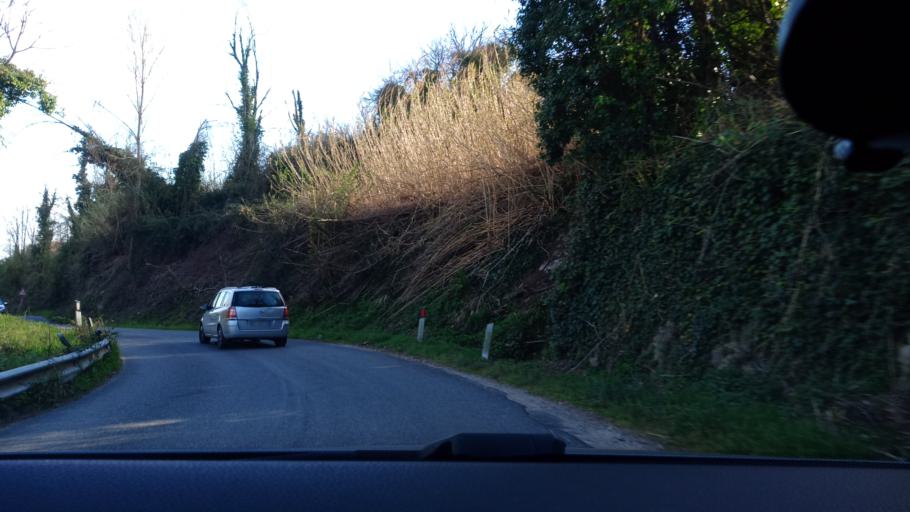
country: IT
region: Latium
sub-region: Citta metropolitana di Roma Capitale
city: Torrita Tiberina
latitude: 42.2399
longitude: 12.6223
